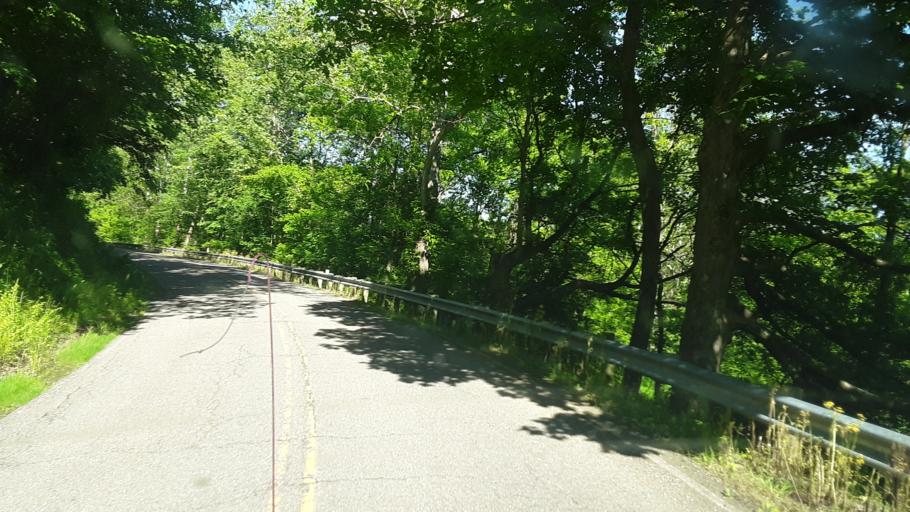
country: US
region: Ohio
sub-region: Tuscarawas County
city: Newcomerstown
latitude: 40.1829
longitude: -81.6110
